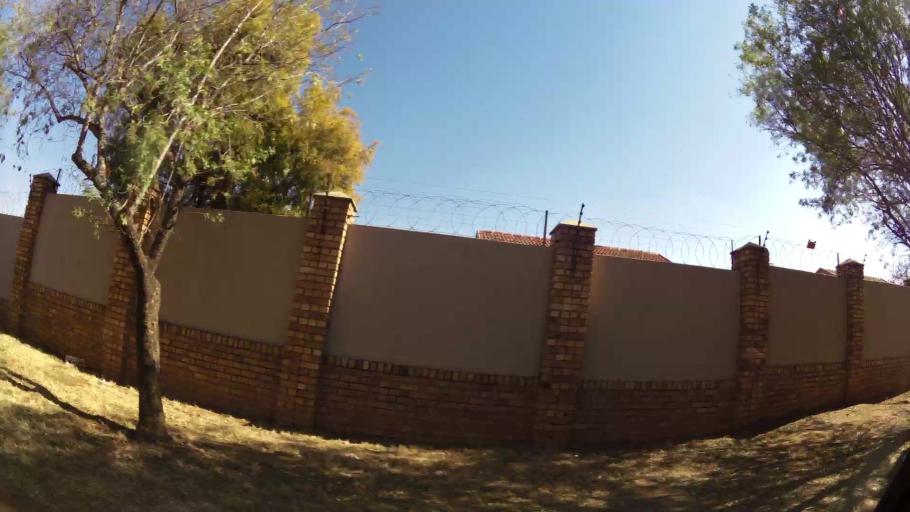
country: ZA
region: Gauteng
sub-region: City of Johannesburg Metropolitan Municipality
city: Johannesburg
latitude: -26.2669
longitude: 28.0144
